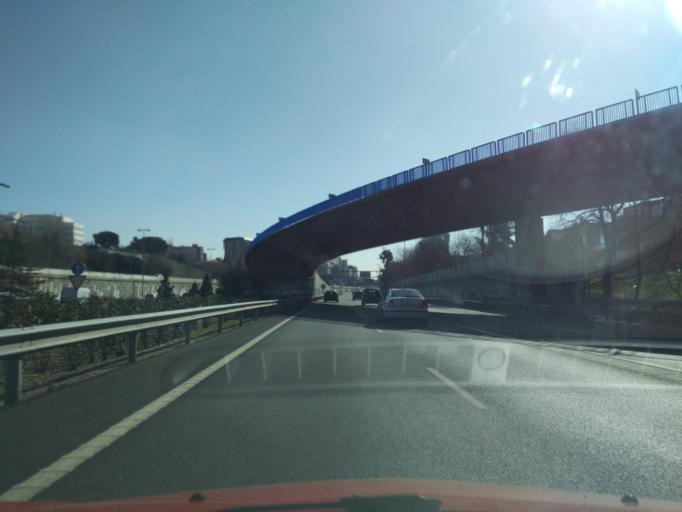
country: ES
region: Madrid
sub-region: Provincia de Madrid
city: Chamartin
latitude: 40.4594
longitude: -3.6651
